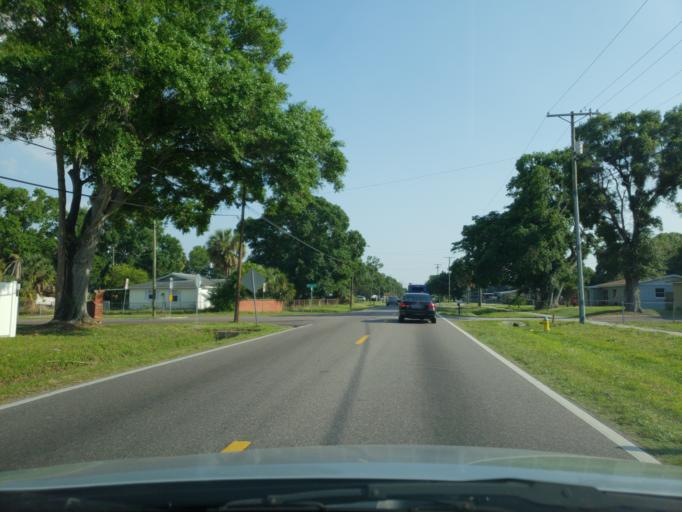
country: US
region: Florida
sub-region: Hillsborough County
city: Palm River-Clair Mel
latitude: 27.9172
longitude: -82.3687
